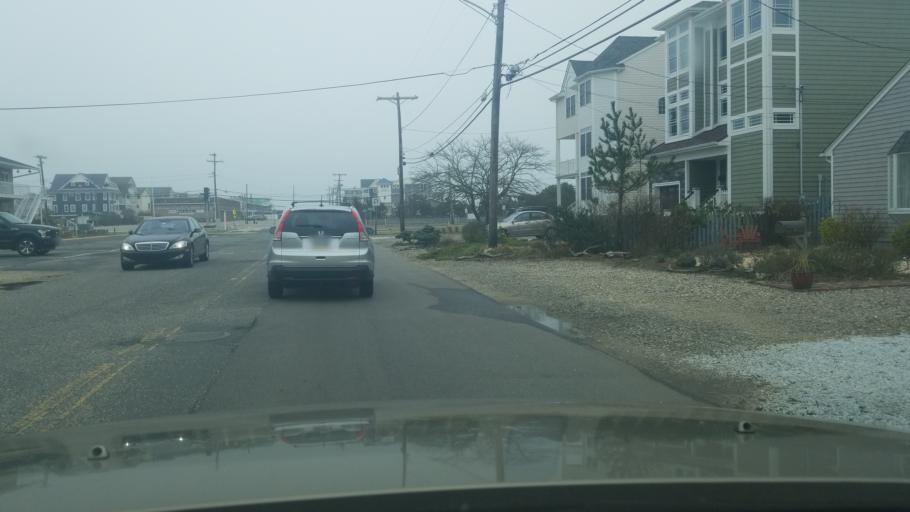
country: US
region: New Jersey
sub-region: Ocean County
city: Seaside Park
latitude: 39.9058
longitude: -74.0825
